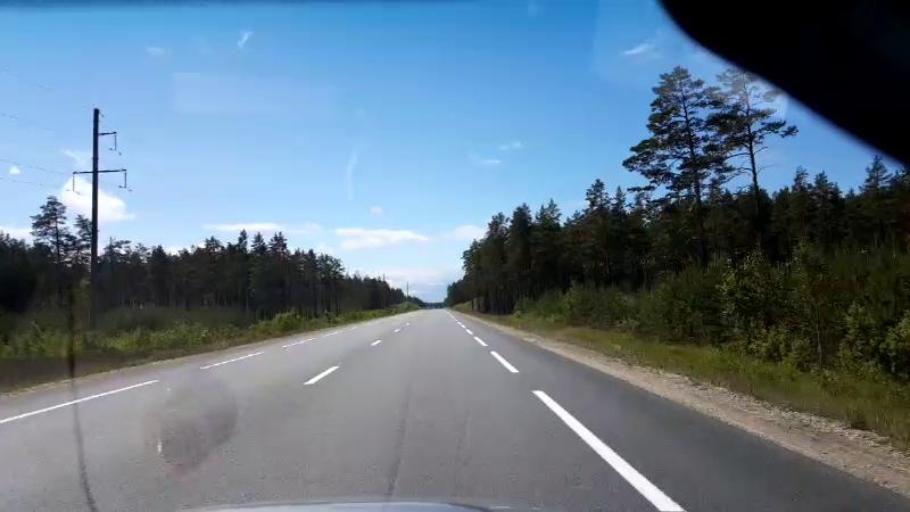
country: LV
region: Saulkrastu
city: Saulkrasti
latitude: 57.2128
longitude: 24.3951
